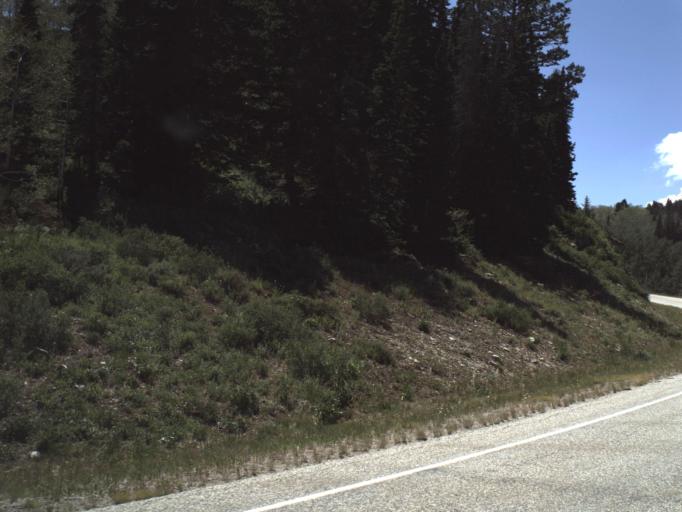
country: US
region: Utah
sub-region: Rich County
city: Randolph
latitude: 41.4750
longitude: -111.4555
